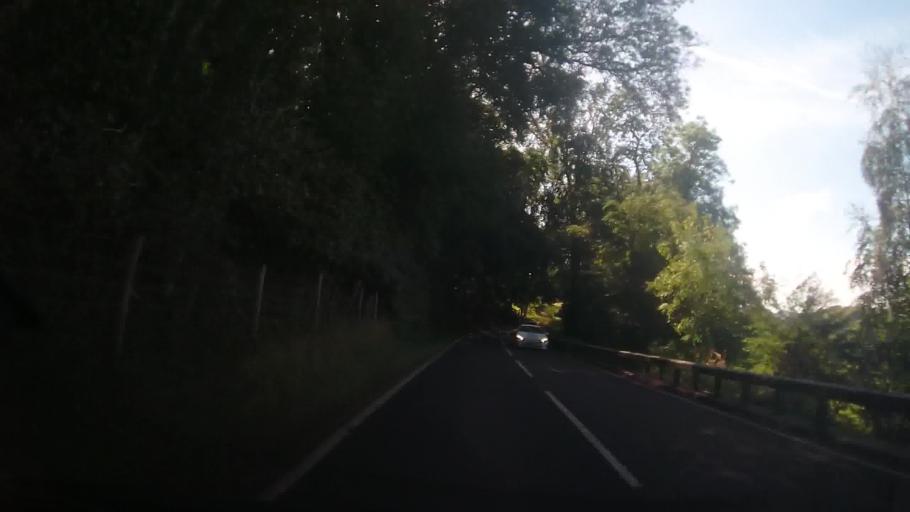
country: GB
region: Wales
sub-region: Sir Powys
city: Mochdre
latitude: 52.4690
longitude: -3.3209
